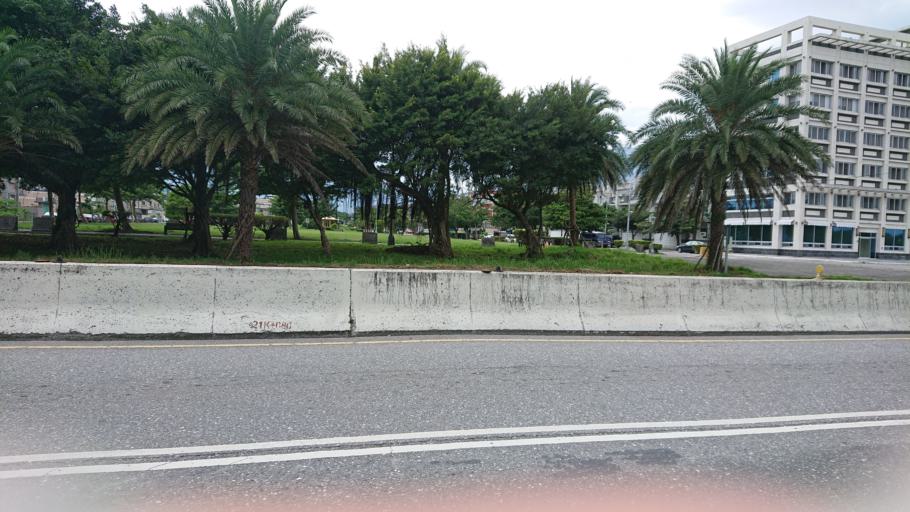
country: TW
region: Taiwan
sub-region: Hualien
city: Hualian
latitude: 23.9391
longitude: 121.5943
